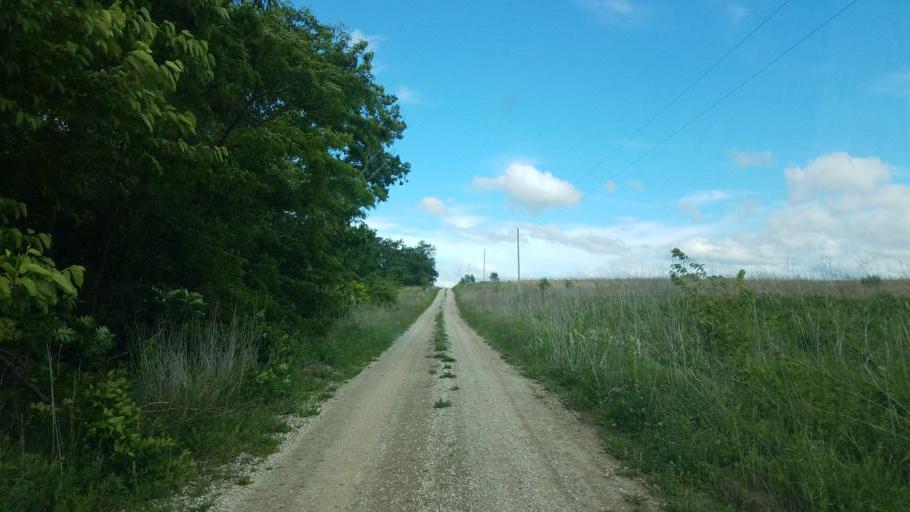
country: US
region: Missouri
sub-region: Mercer County
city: Princeton
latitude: 40.2602
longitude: -93.7040
